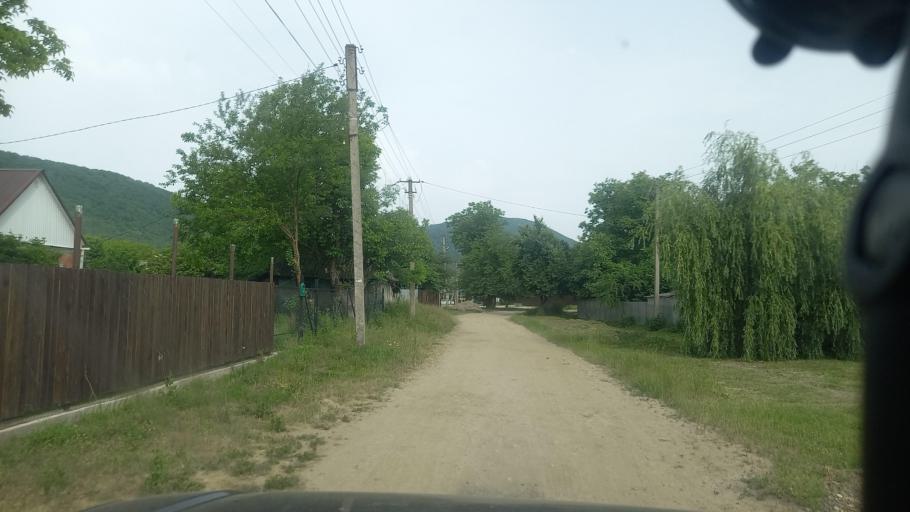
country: RU
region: Krasnodarskiy
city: Goryachiy Klyuch
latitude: 44.6043
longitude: 39.0309
